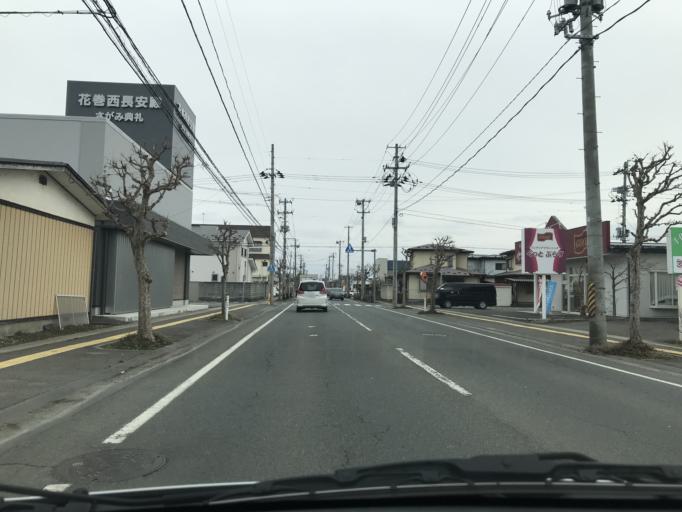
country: JP
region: Iwate
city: Hanamaki
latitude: 39.3920
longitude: 141.1080
